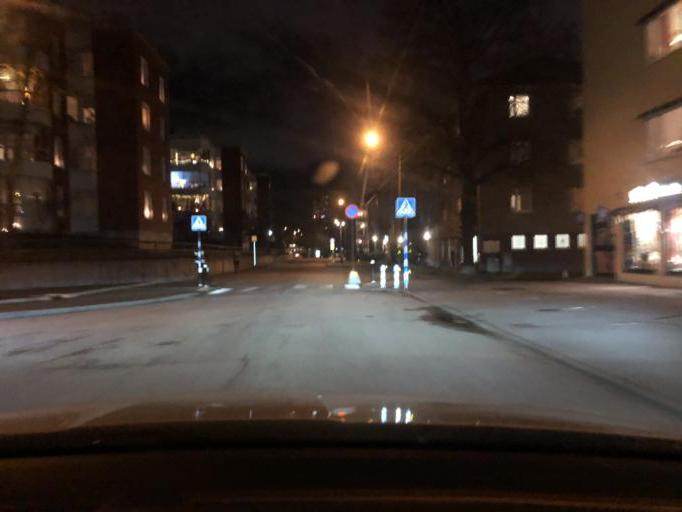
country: SE
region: Vaermland
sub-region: Karlstads Kommun
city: Karlstad
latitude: 59.3758
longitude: 13.4883
